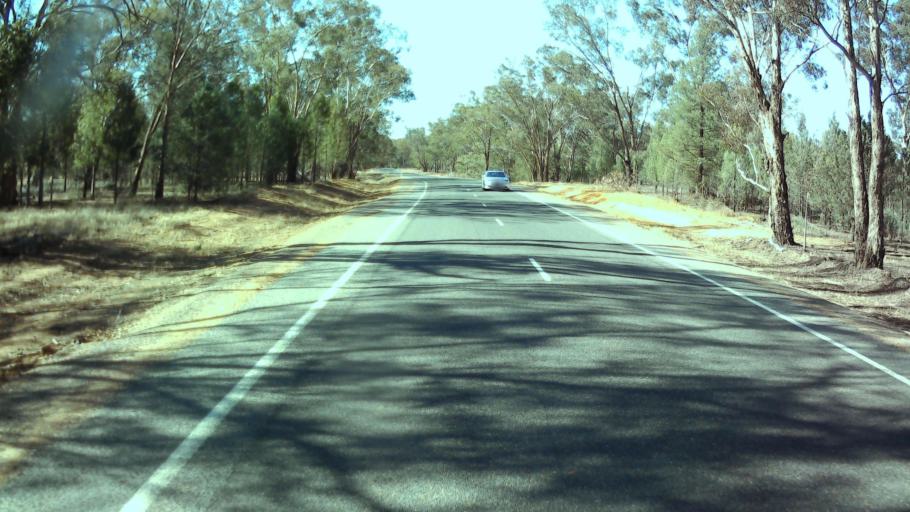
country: AU
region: New South Wales
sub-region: Weddin
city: Grenfell
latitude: -33.7593
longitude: 148.0825
